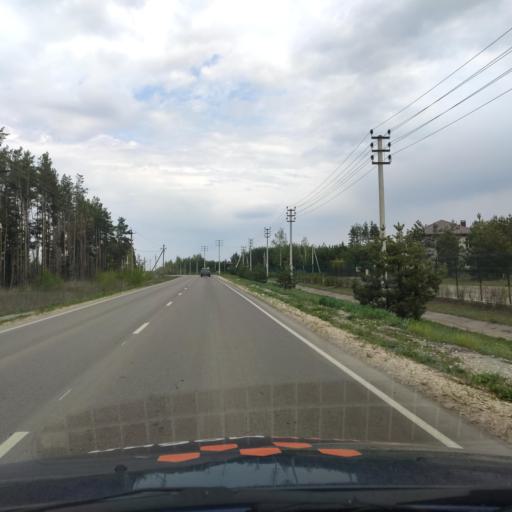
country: RU
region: Voronezj
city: Podgornoye
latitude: 51.8565
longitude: 39.1608
